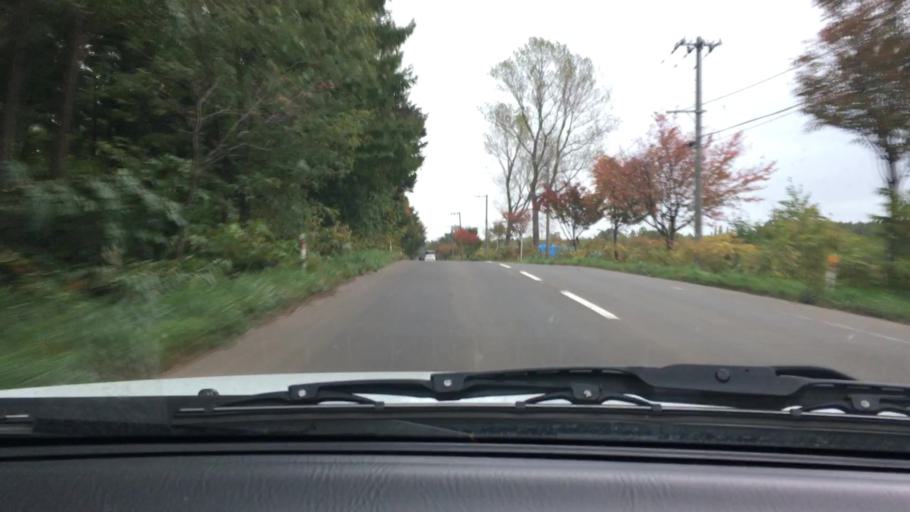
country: JP
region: Aomori
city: Shimokizukuri
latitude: 40.7168
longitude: 140.3122
